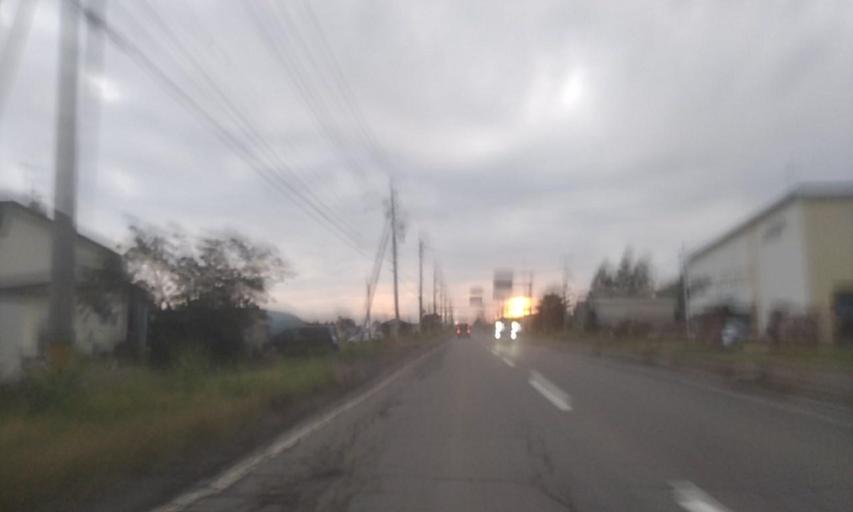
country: JP
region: Hokkaido
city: Abashiri
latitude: 43.9014
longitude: 144.6780
